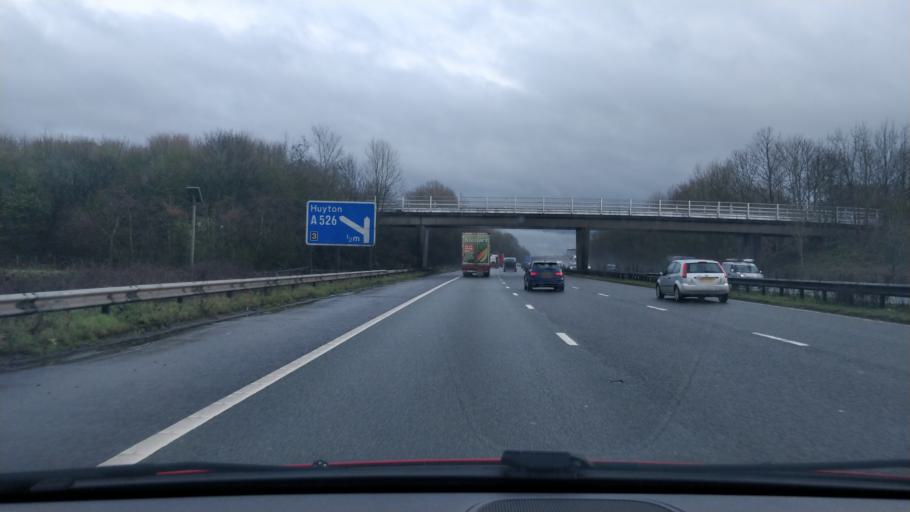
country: GB
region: England
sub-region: Knowsley
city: Knowsley
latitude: 53.4465
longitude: -2.8603
